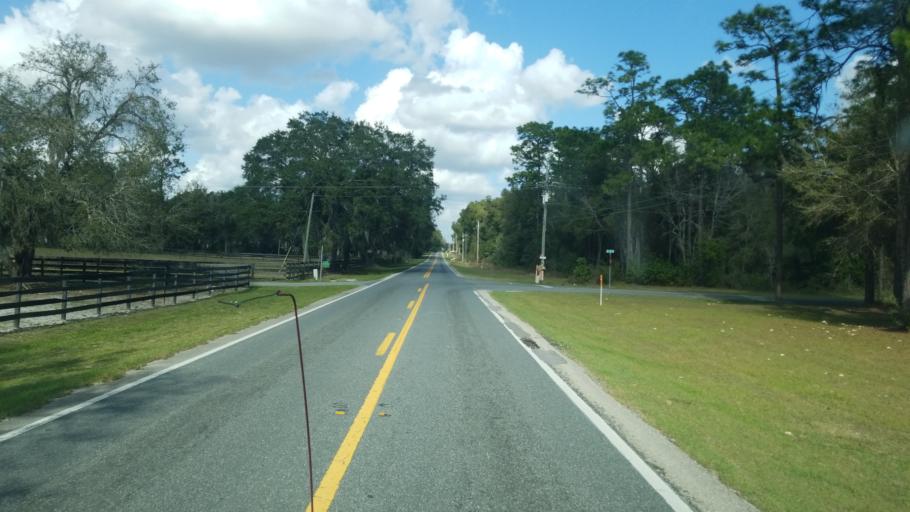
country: US
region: Florida
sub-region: Marion County
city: Belleview
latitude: 28.9623
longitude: -82.1199
